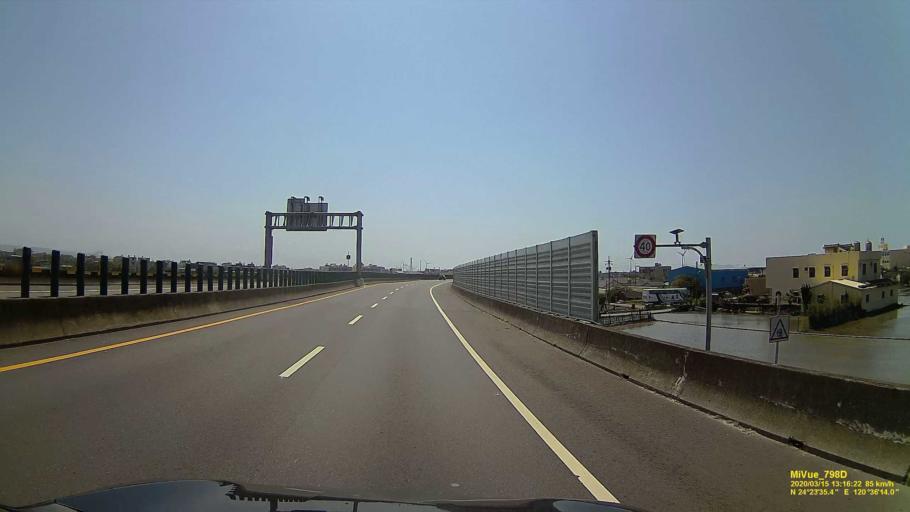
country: TW
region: Taiwan
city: Fengyuan
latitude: 24.3925
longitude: 120.6024
